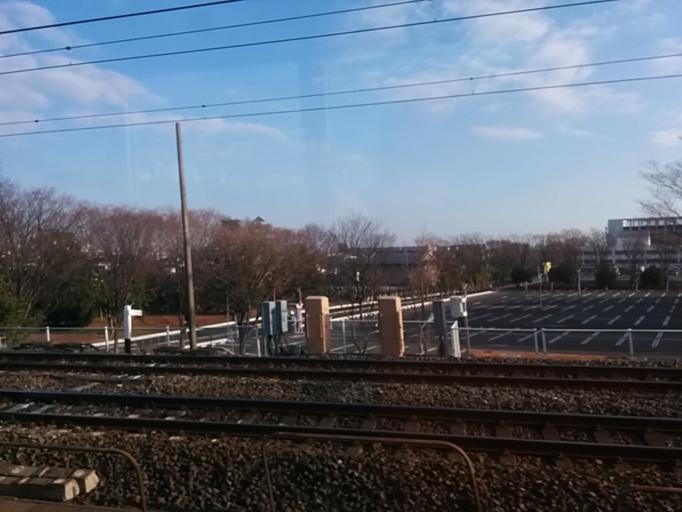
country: JP
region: Saitama
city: Asaka
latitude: 35.8112
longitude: 139.5921
